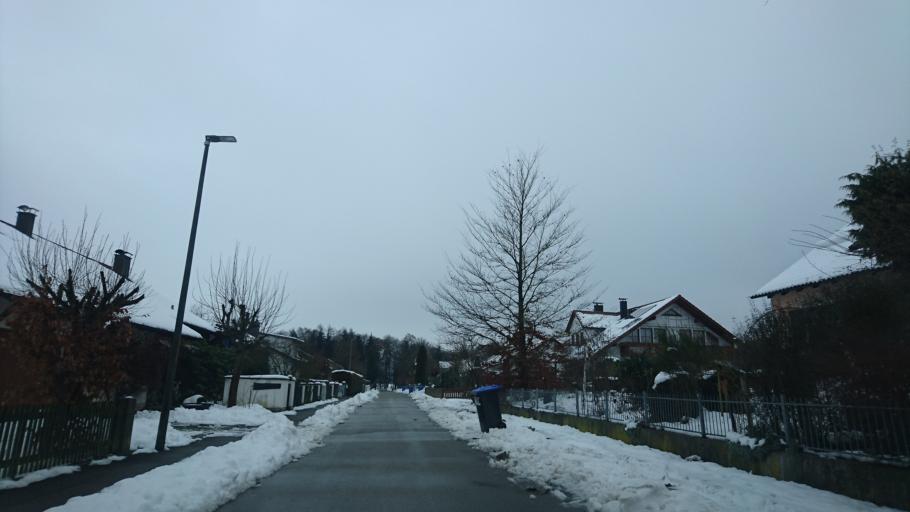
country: DE
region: Bavaria
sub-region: Swabia
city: Landensberg
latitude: 48.4354
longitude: 10.5132
